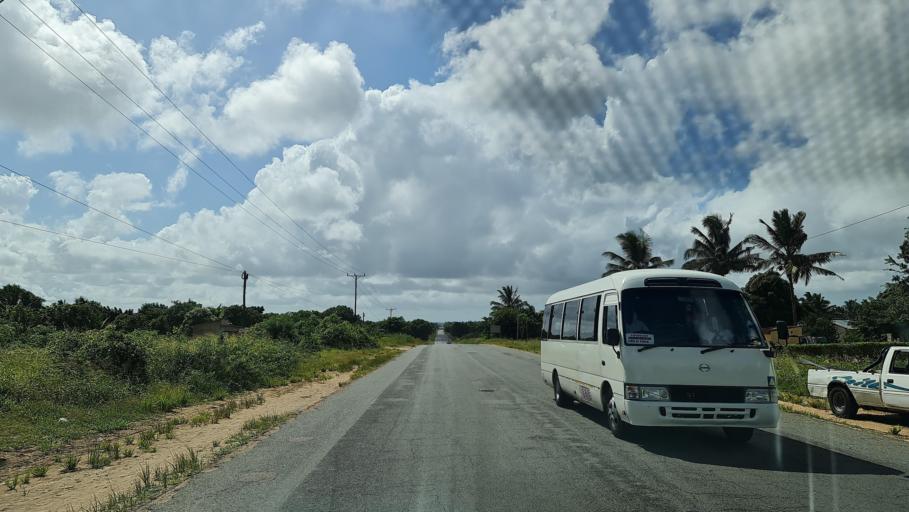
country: MZ
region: Gaza
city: Manjacaze
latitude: -24.6752
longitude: 34.5822
